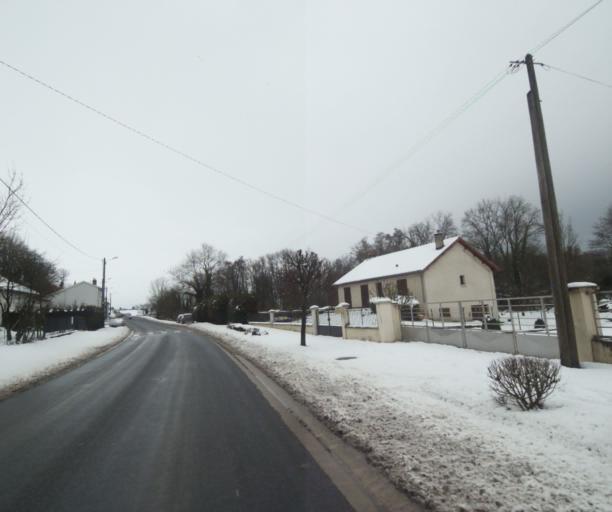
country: FR
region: Champagne-Ardenne
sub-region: Departement de la Haute-Marne
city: Wassy
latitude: 48.4758
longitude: 4.9703
